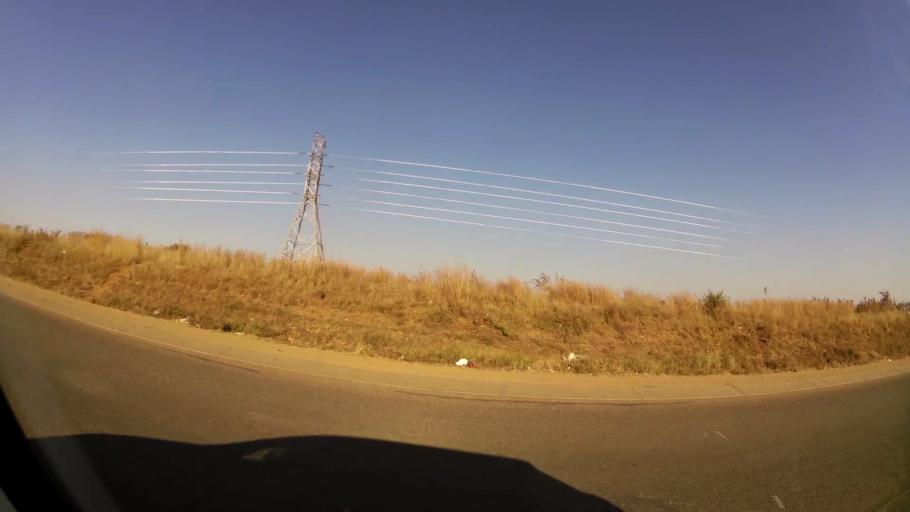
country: ZA
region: Gauteng
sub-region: City of Tshwane Metropolitan Municipality
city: Cullinan
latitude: -25.7327
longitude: 28.3981
